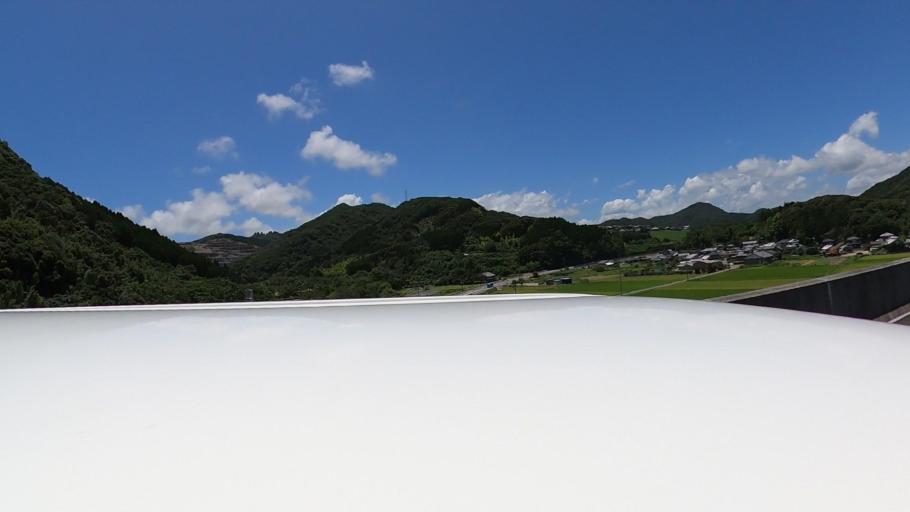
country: JP
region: Miyazaki
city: Nobeoka
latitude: 32.3971
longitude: 131.6191
